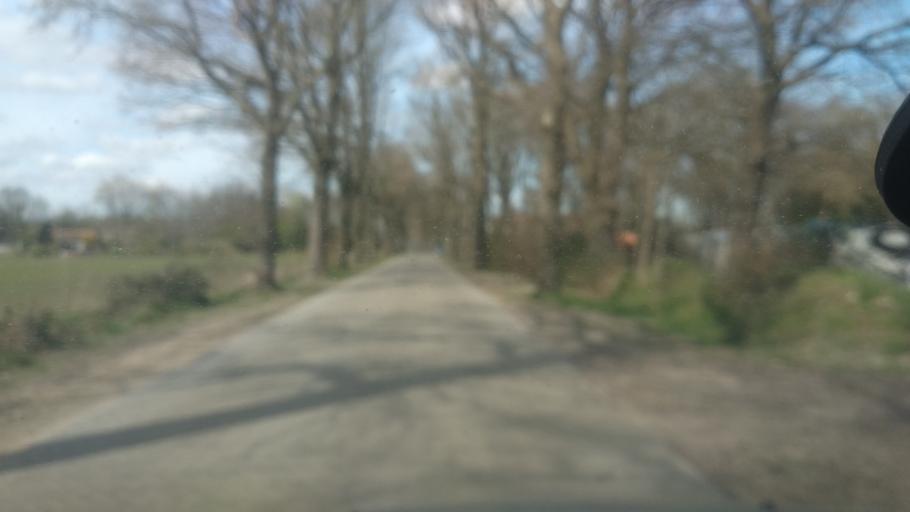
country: NL
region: Drenthe
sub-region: Gemeente Borger-Odoorn
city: Borger
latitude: 52.9559
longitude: 6.8243
